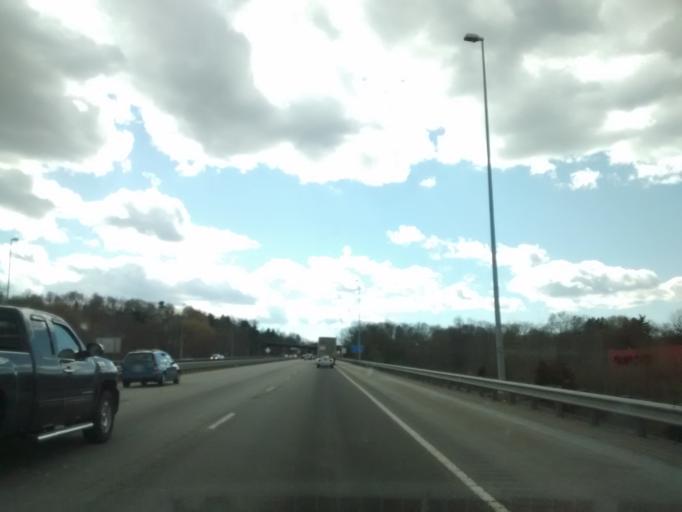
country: US
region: Massachusetts
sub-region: Worcester County
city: Hamilton
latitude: 42.2913
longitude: -71.7734
